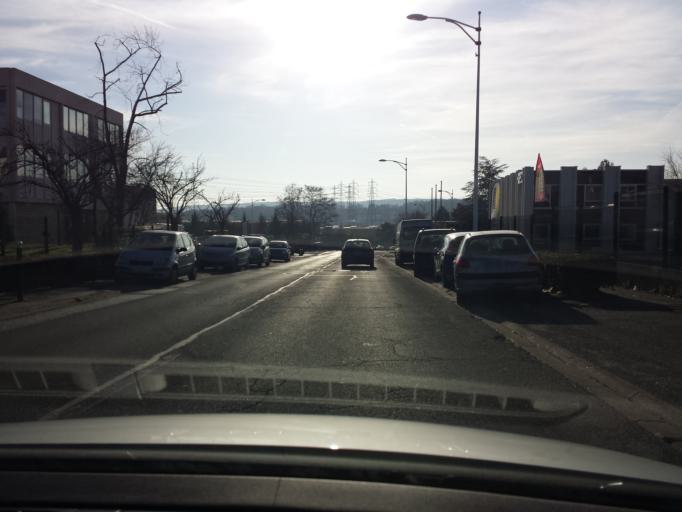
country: FR
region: Ile-de-France
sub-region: Departement de l'Essonne
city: Palaiseau
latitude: 48.7117
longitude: 2.2569
